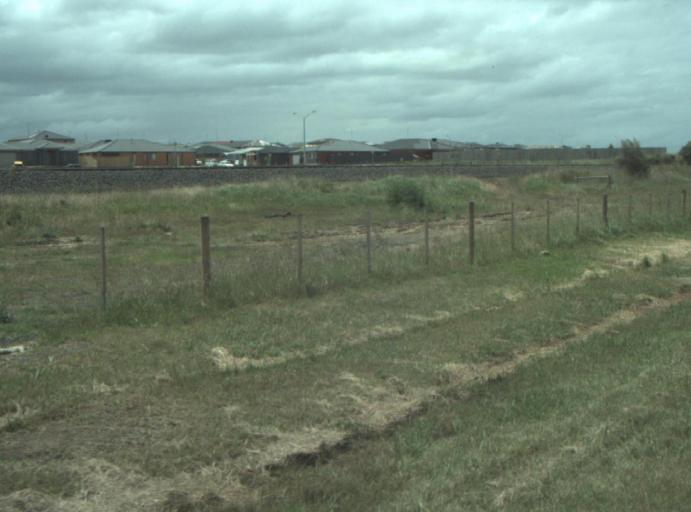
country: AU
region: Victoria
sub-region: Greater Geelong
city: Wandana Heights
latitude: -38.2167
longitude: 144.3031
